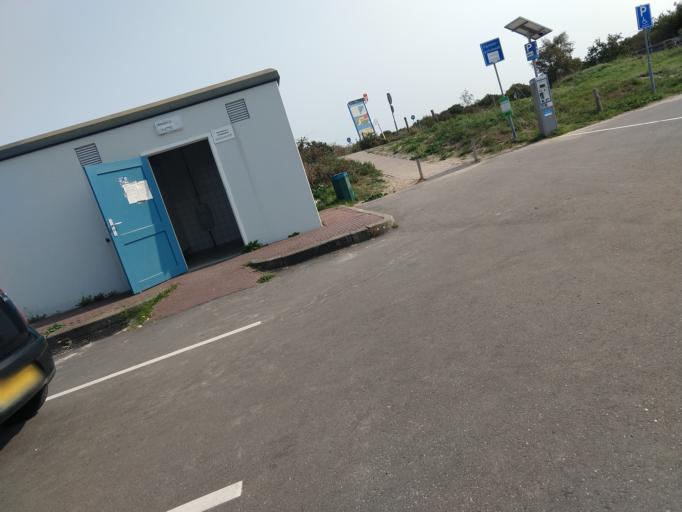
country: NL
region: Zeeland
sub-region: Schouwen-Duiveland
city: Renesse
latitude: 51.7410
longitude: 3.7745
